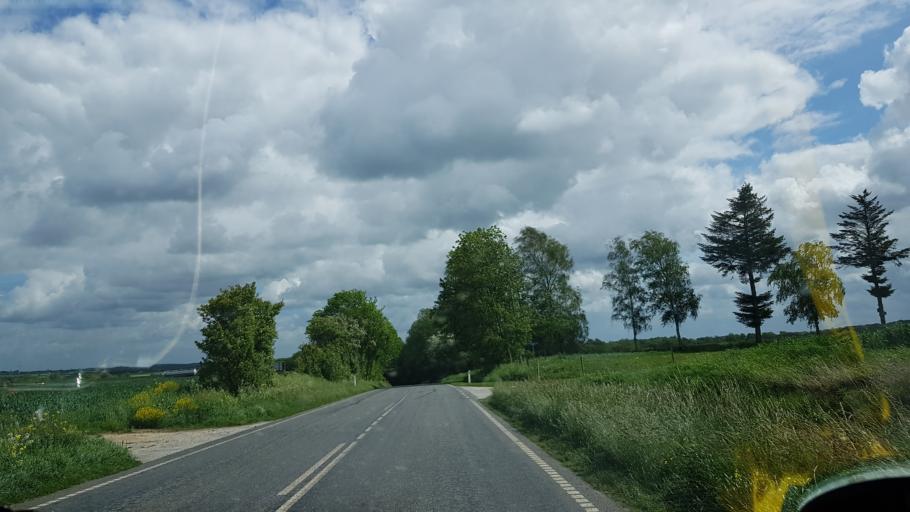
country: DK
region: South Denmark
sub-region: Kolding Kommune
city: Christiansfeld
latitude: 55.3317
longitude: 9.4382
